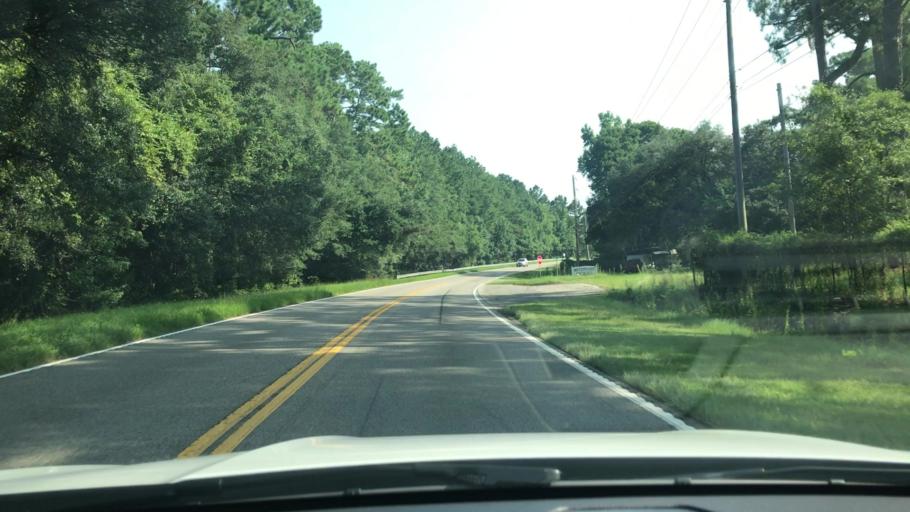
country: US
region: South Carolina
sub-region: Georgetown County
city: Georgetown
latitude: 33.4744
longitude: -79.2787
